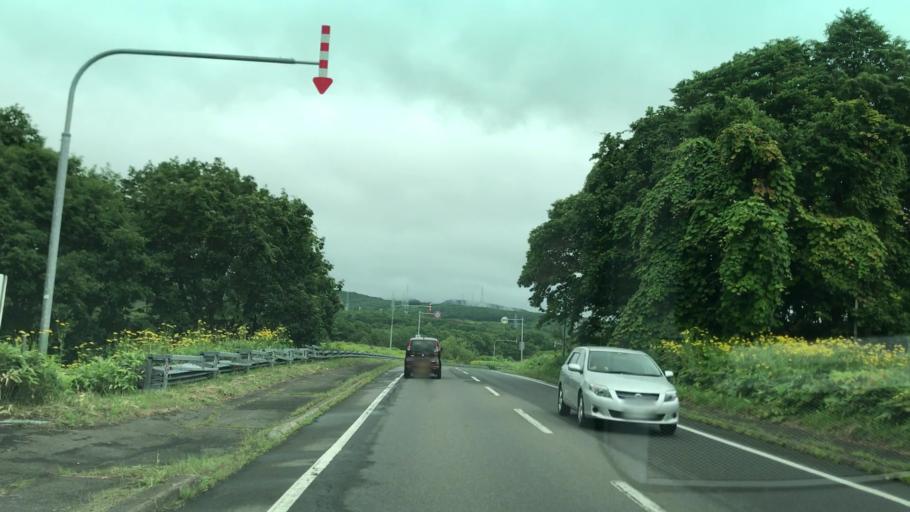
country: JP
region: Hokkaido
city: Muroran
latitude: 42.3882
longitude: 140.9859
